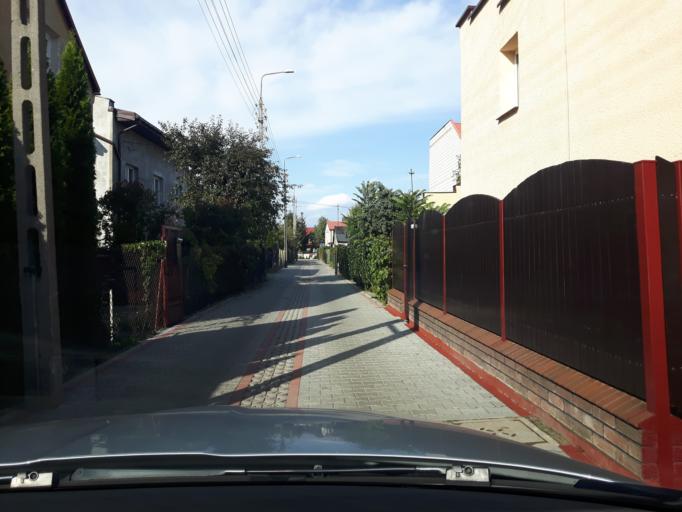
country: PL
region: Masovian Voivodeship
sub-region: Powiat wolominski
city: Zabki
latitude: 52.2874
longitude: 21.0965
